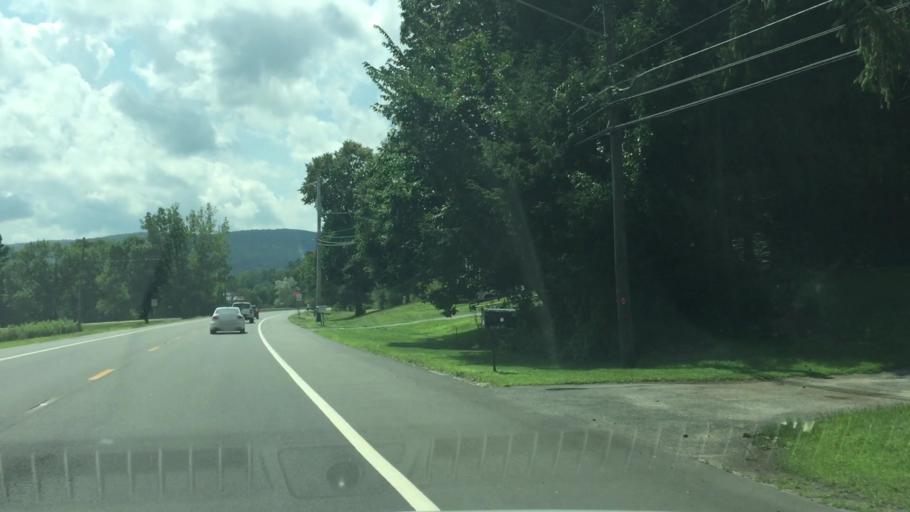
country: US
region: Massachusetts
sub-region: Berkshire County
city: Lee
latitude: 42.2885
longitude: -73.2433
